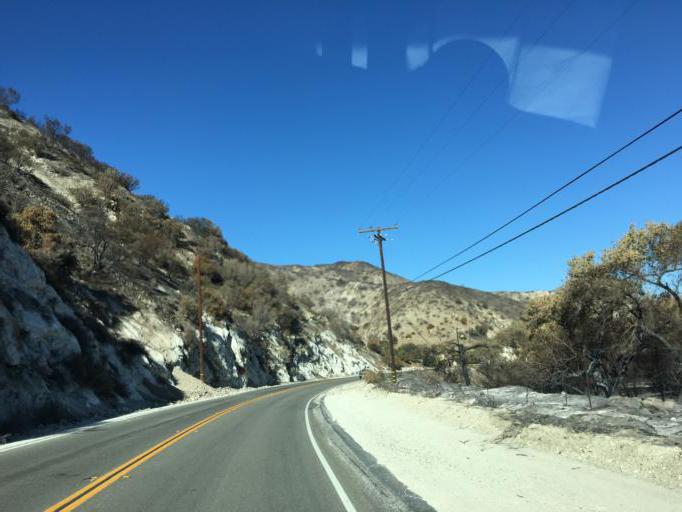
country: US
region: California
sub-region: Los Angeles County
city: Agua Dulce
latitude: 34.4376
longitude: -118.3003
